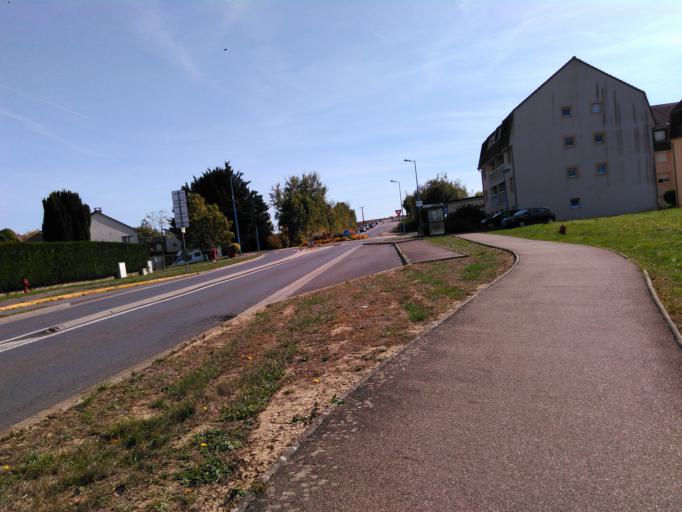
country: FR
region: Lorraine
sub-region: Departement de la Moselle
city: Hettange-Grande
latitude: 49.3942
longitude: 6.1657
